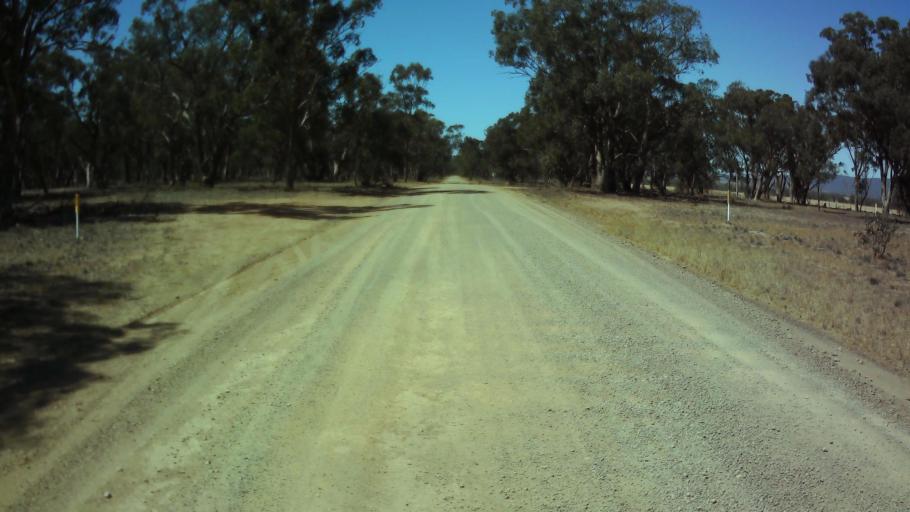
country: AU
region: New South Wales
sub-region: Weddin
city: Grenfell
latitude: -33.8495
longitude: 148.0886
